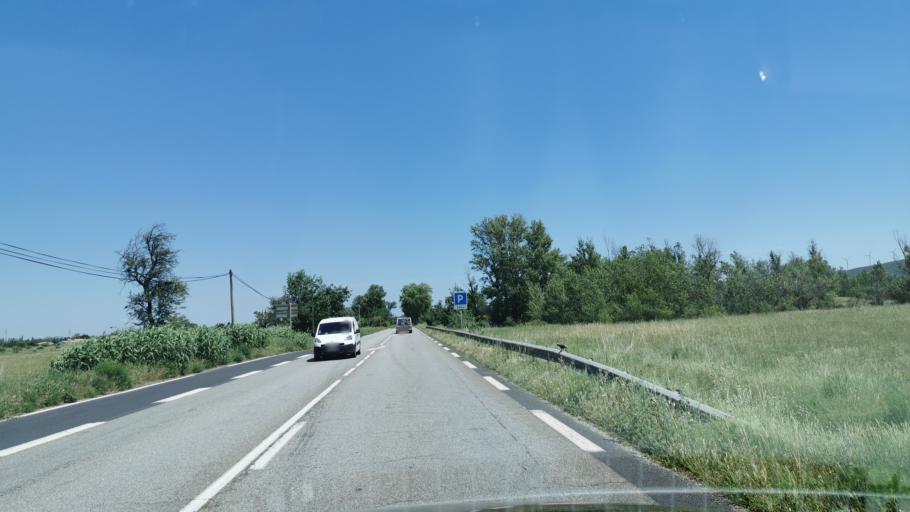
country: FR
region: Languedoc-Roussillon
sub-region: Departement de l'Aude
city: Canet
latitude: 43.2126
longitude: 2.8442
